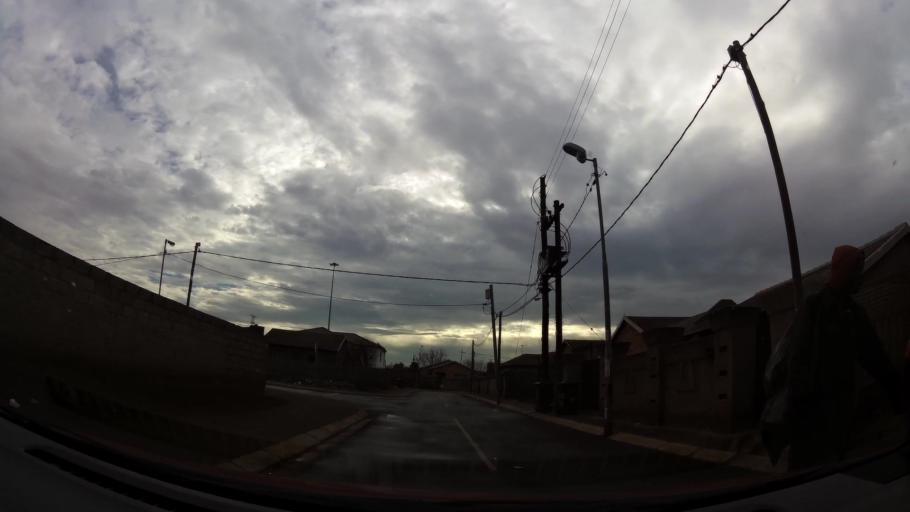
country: ZA
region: Gauteng
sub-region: City of Johannesburg Metropolitan Municipality
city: Soweto
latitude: -26.2831
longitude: 27.8446
